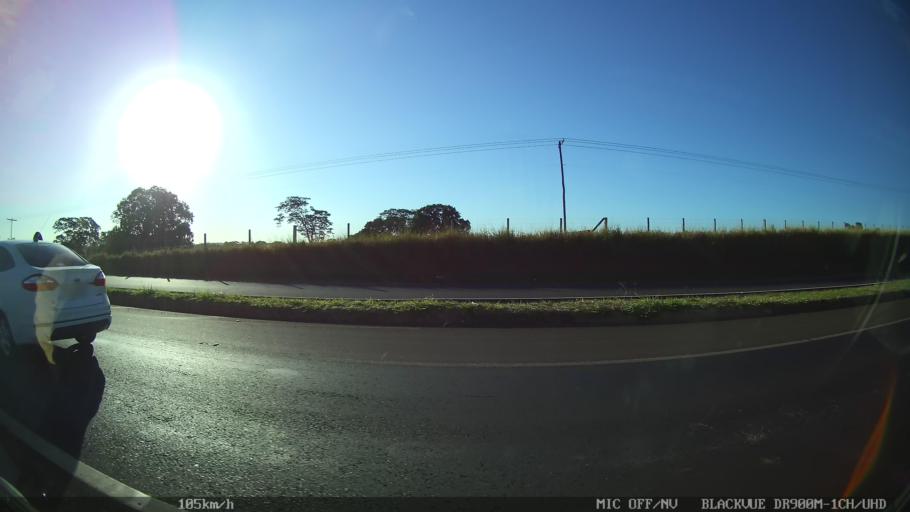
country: BR
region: Sao Paulo
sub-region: Guapiacu
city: Guapiacu
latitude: -20.7861
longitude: -49.2781
